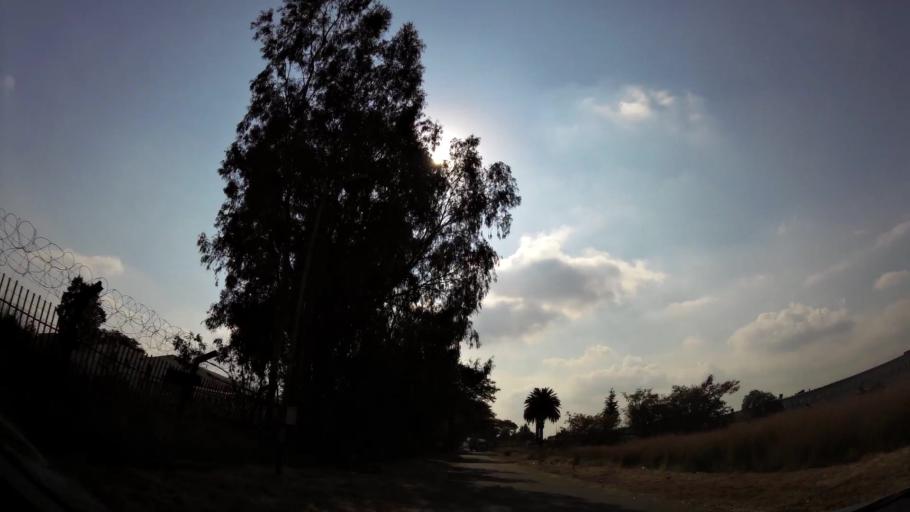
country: ZA
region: Gauteng
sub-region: Ekurhuleni Metropolitan Municipality
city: Boksburg
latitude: -26.1621
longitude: 28.2062
